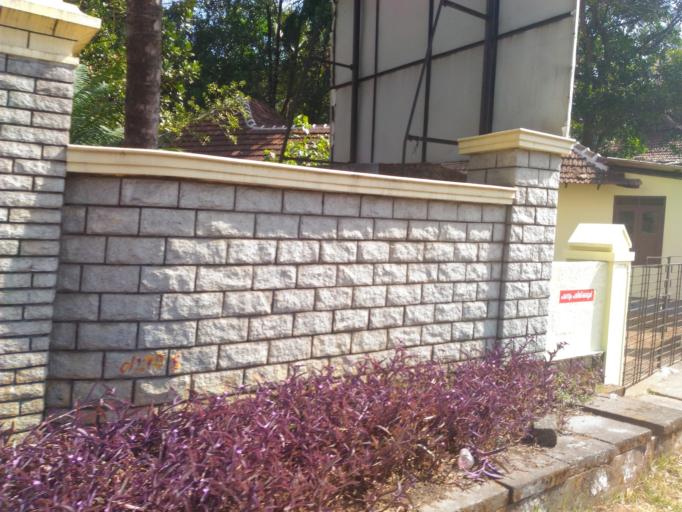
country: IN
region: Kerala
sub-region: Kottayam
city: Lalam
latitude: 9.7123
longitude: 76.6910
